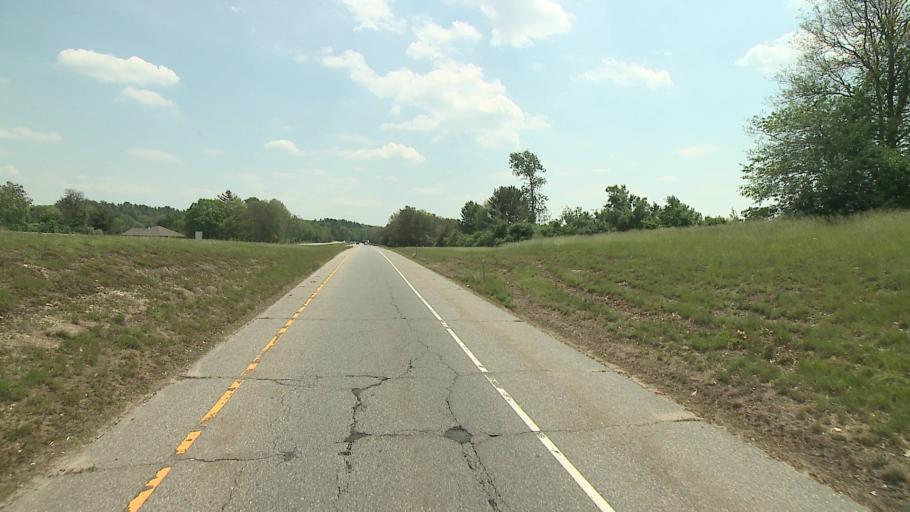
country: US
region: Connecticut
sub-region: Windham County
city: Killingly Center
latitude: 41.8414
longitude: -71.8794
